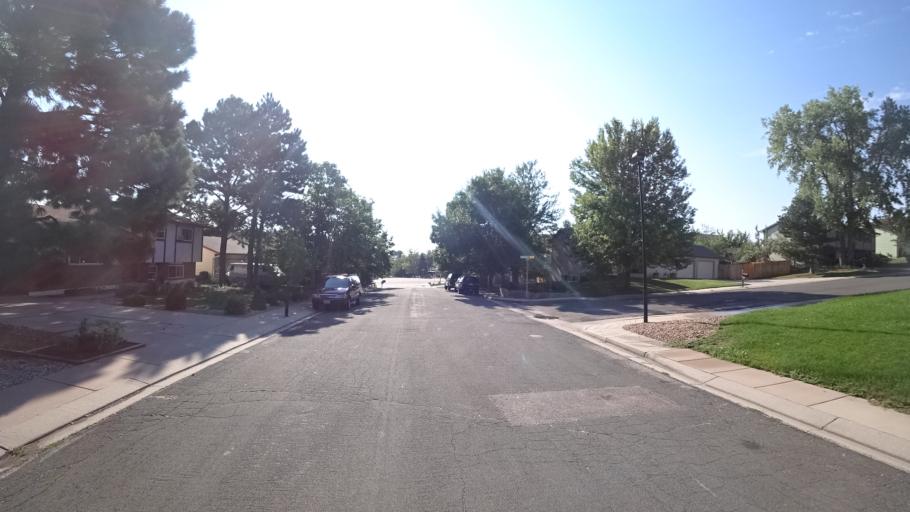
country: US
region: Colorado
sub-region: El Paso County
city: Colorado Springs
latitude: 38.8855
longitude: -104.8487
